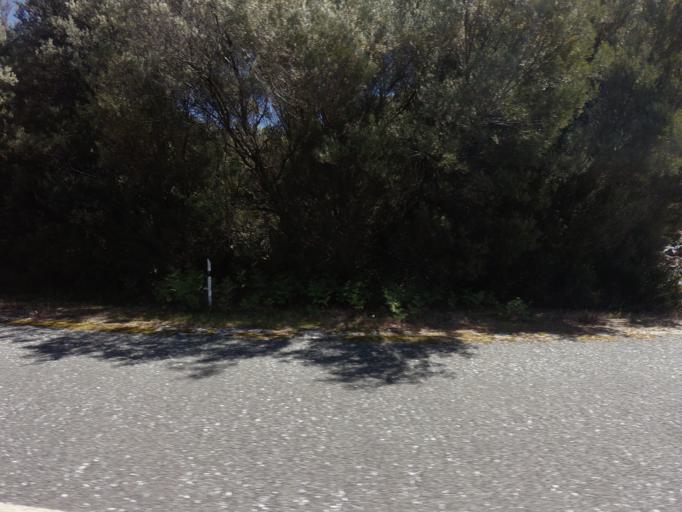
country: AU
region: Tasmania
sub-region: West Coast
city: Queenstown
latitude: -42.7567
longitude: 146.0024
